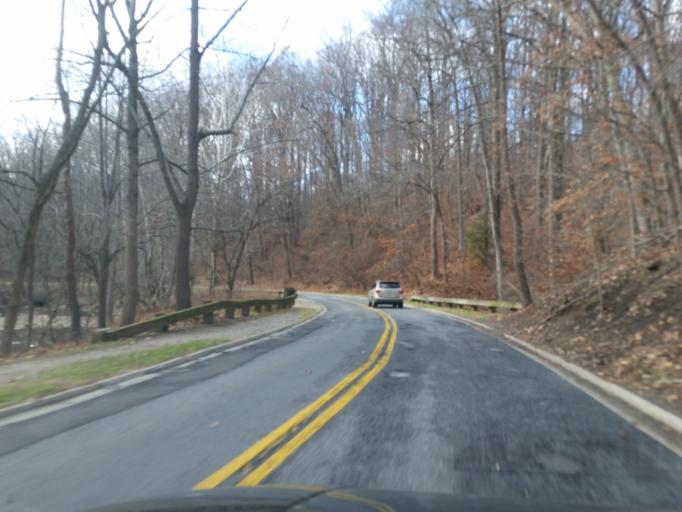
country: US
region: Maryland
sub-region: Montgomery County
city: Silver Spring
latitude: 38.9714
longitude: -77.0434
